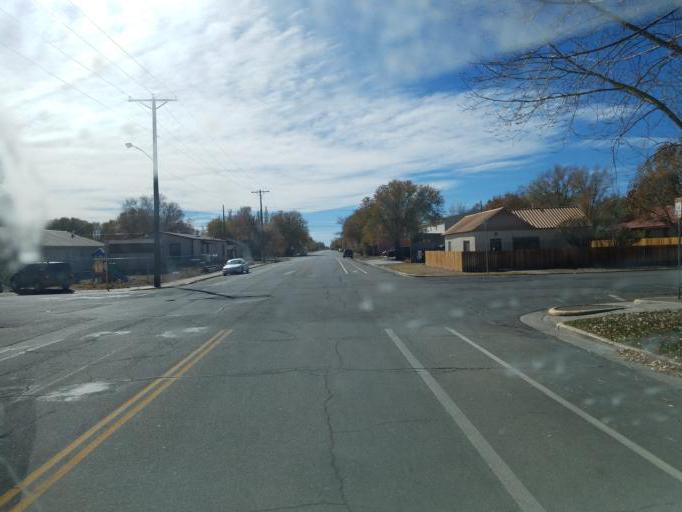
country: US
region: Colorado
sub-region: Alamosa County
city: Alamosa
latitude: 37.4637
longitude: -105.8702
